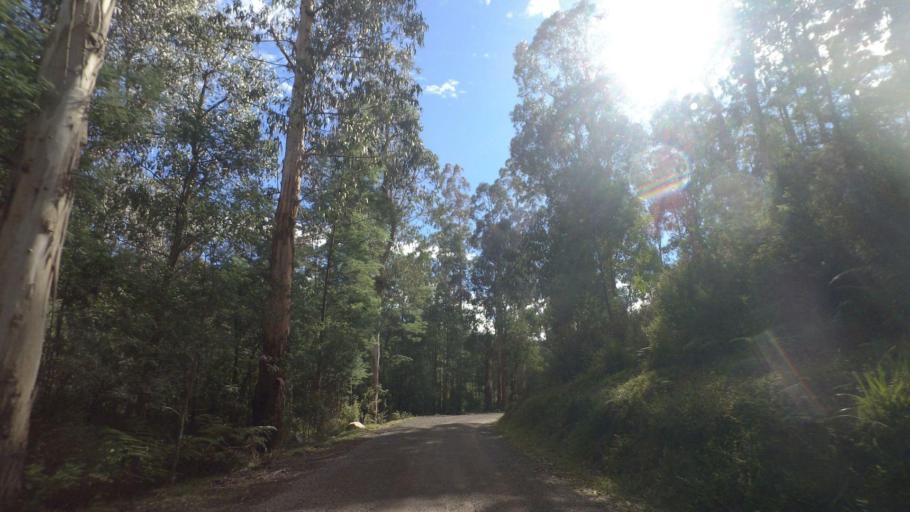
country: AU
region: Victoria
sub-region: Cardinia
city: Bunyip
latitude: -37.9809
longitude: 145.8114
